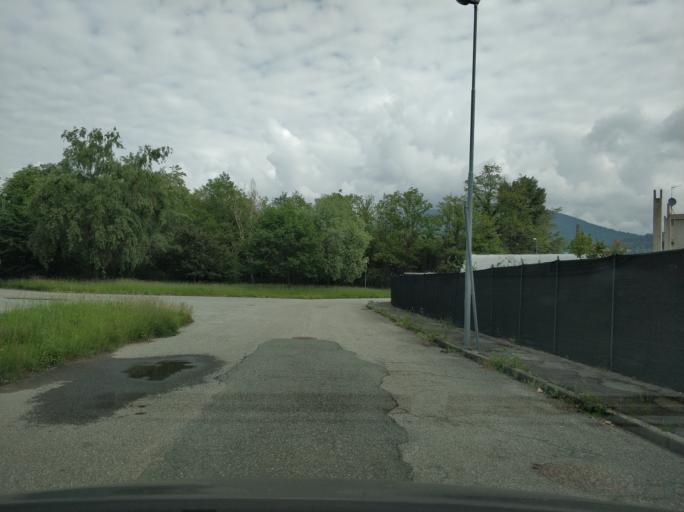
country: IT
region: Piedmont
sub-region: Provincia di Torino
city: Balangero
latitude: 45.2672
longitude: 7.5014
